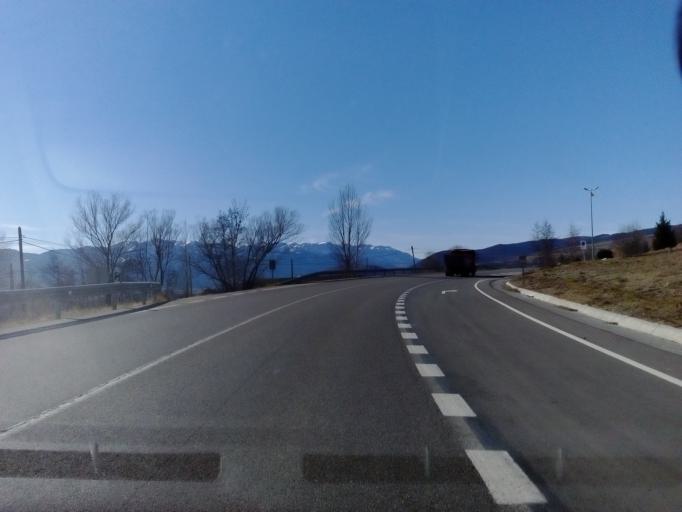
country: ES
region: Catalonia
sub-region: Provincia de Girona
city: Bolvir
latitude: 42.4160
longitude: 1.8775
